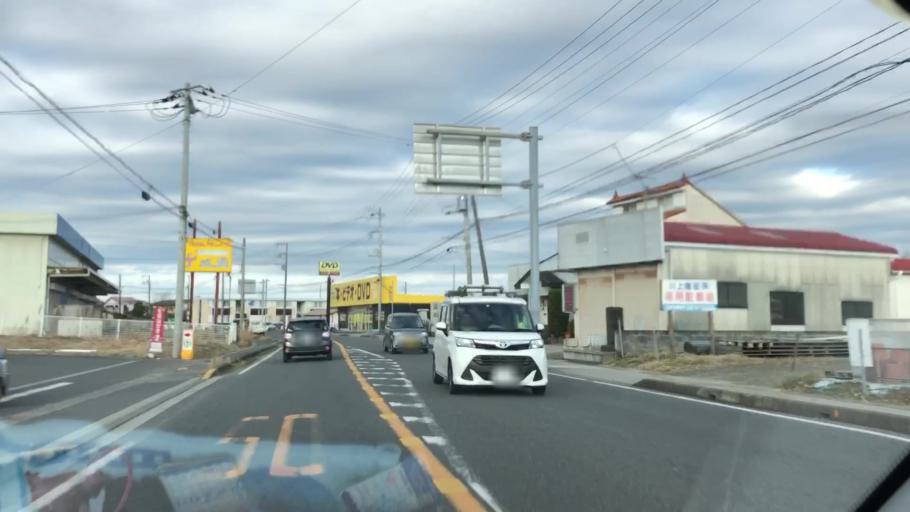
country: JP
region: Chiba
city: Tateyama
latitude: 34.9992
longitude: 139.9067
